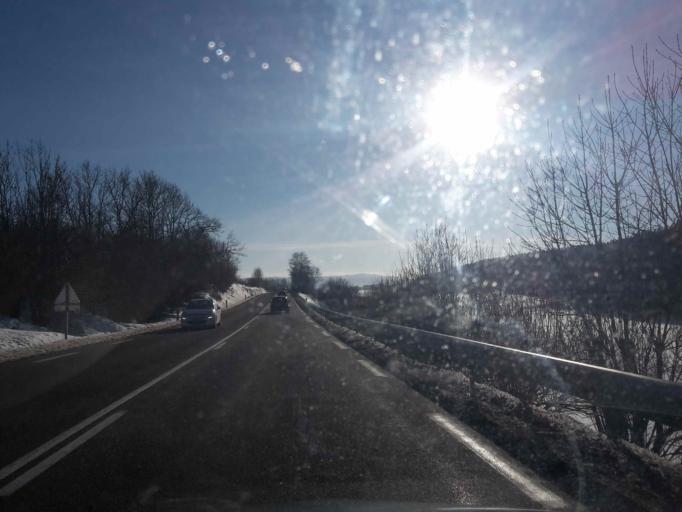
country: FR
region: Franche-Comte
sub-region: Departement du Doubs
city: Doubs
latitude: 46.9651
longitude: 6.3447
